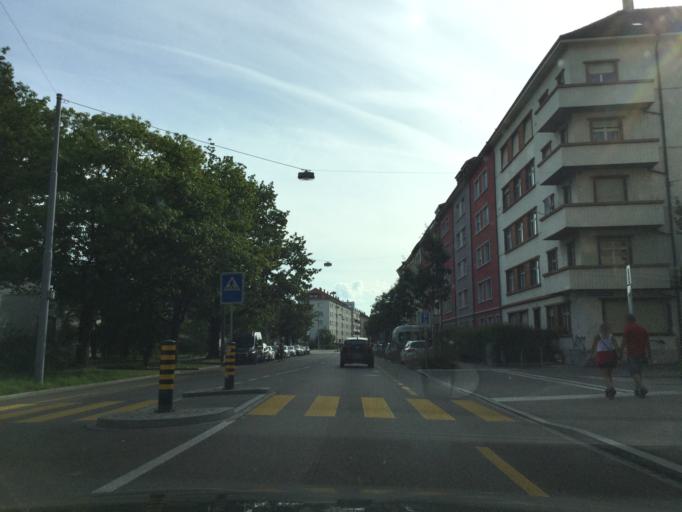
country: CH
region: Basel-Landschaft
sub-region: Bezirk Arlesheim
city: Birsfelden
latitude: 47.5649
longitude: 7.6056
